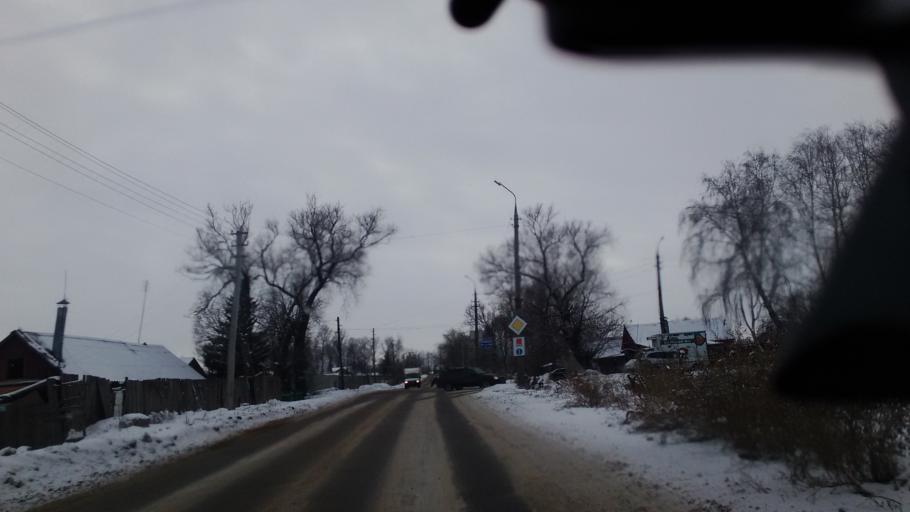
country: RU
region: Tula
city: Bogoroditsk
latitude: 53.7661
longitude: 38.1106
